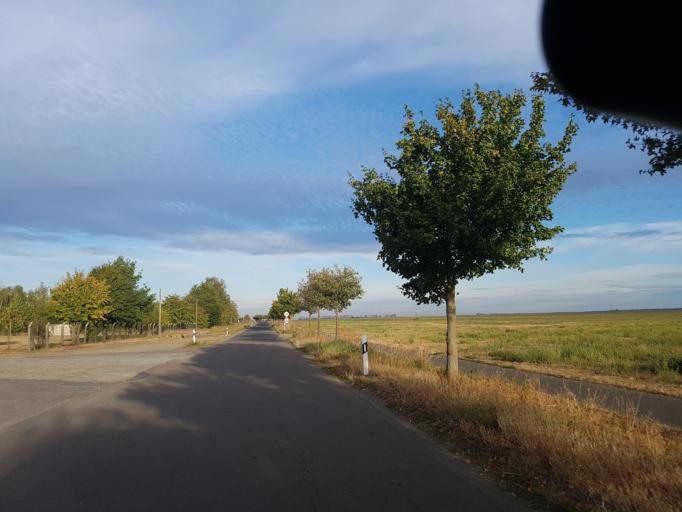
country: DE
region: Brandenburg
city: Dahme
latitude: 51.8580
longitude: 13.4121
